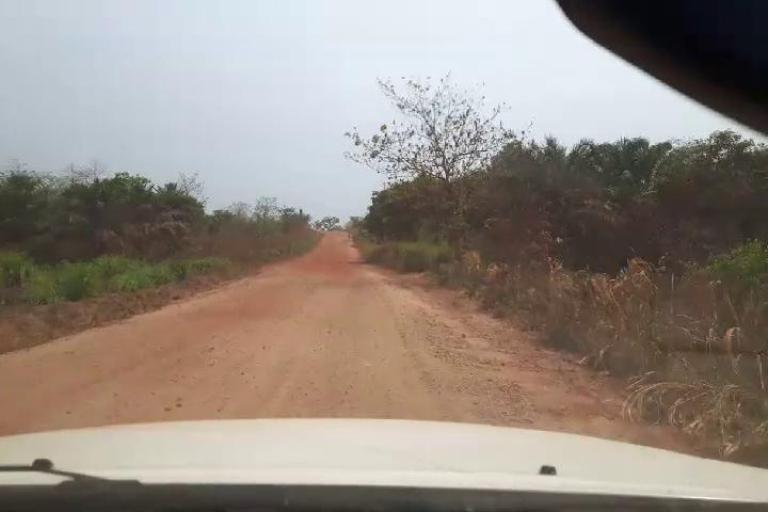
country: SL
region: Northern Province
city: Bumbuna
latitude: 9.0288
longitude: -11.7630
